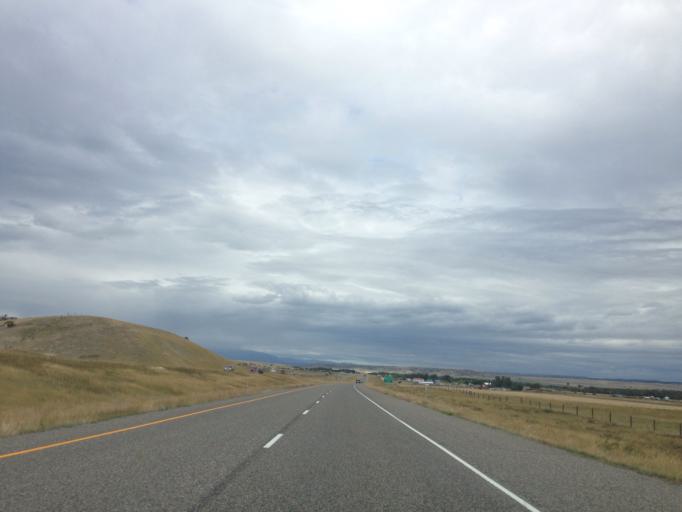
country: US
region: Montana
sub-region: Sweet Grass County
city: Big Timber
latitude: 45.7515
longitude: -109.7776
